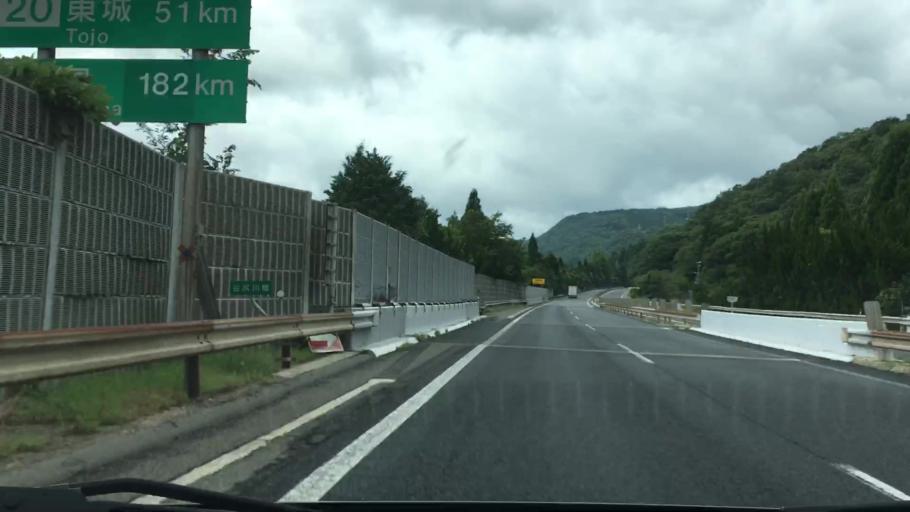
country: JP
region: Okayama
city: Niimi
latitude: 34.9681
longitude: 133.6465
